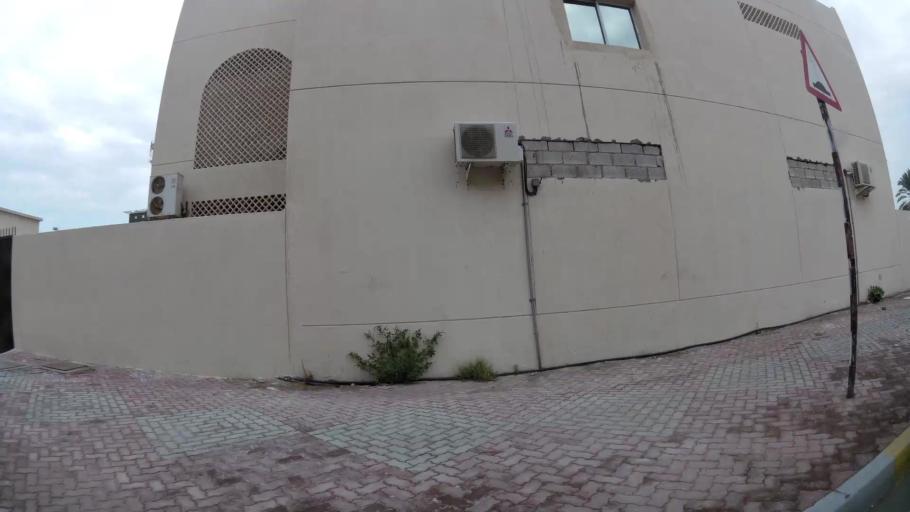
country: AE
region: Abu Dhabi
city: Abu Dhabi
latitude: 24.4449
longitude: 54.3998
